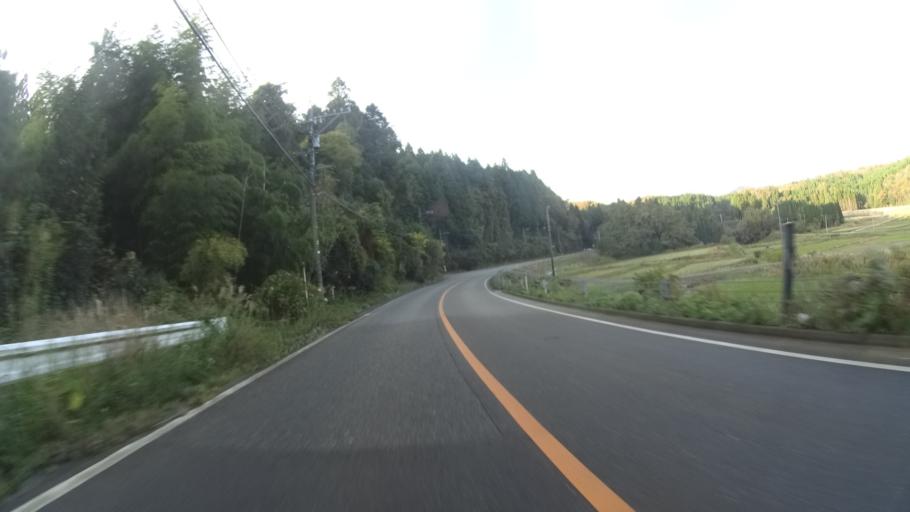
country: JP
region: Ishikawa
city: Nanao
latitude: 37.1778
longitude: 136.7134
